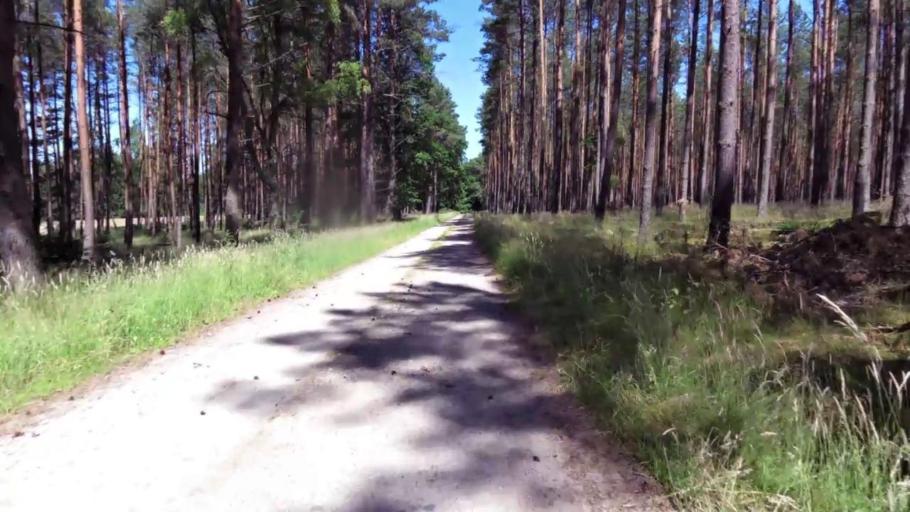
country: PL
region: West Pomeranian Voivodeship
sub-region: Powiat bialogardzki
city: Tychowo
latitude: 53.9266
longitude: 16.1210
